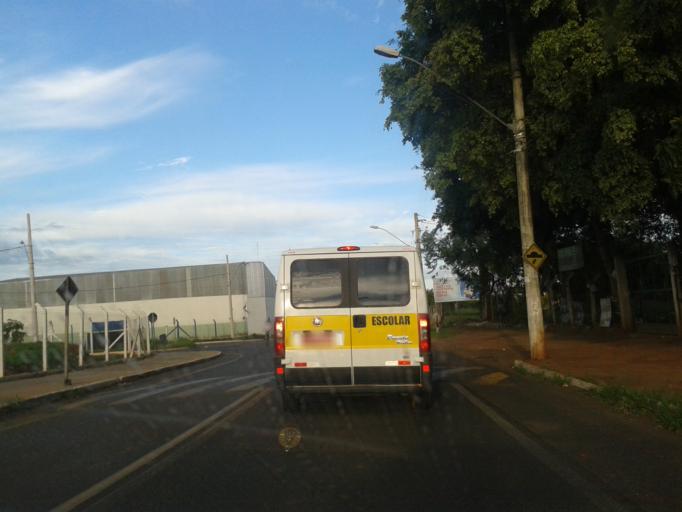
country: BR
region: Minas Gerais
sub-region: Araguari
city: Araguari
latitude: -18.6424
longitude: -48.2140
